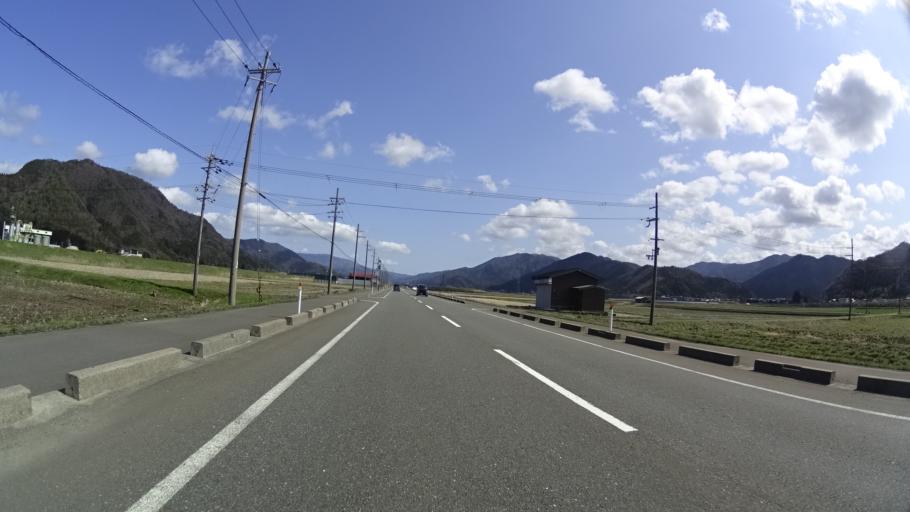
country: JP
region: Fukui
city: Obama
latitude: 35.4862
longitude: 135.7907
